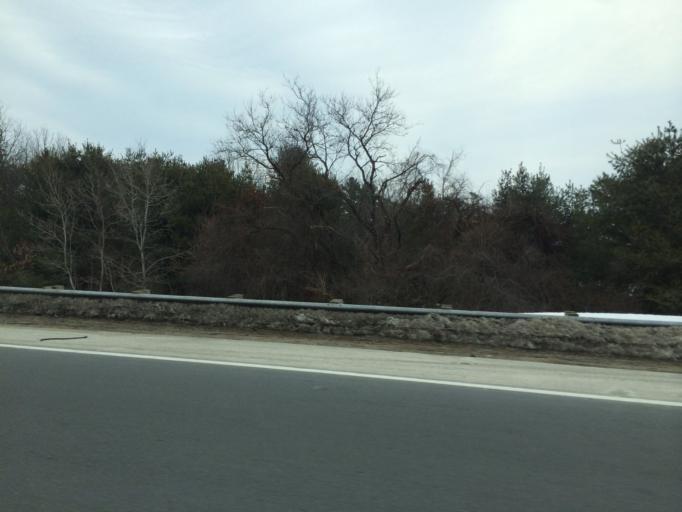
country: US
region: New Hampshire
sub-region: Rockingham County
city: Derry
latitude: 42.8736
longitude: -71.3420
